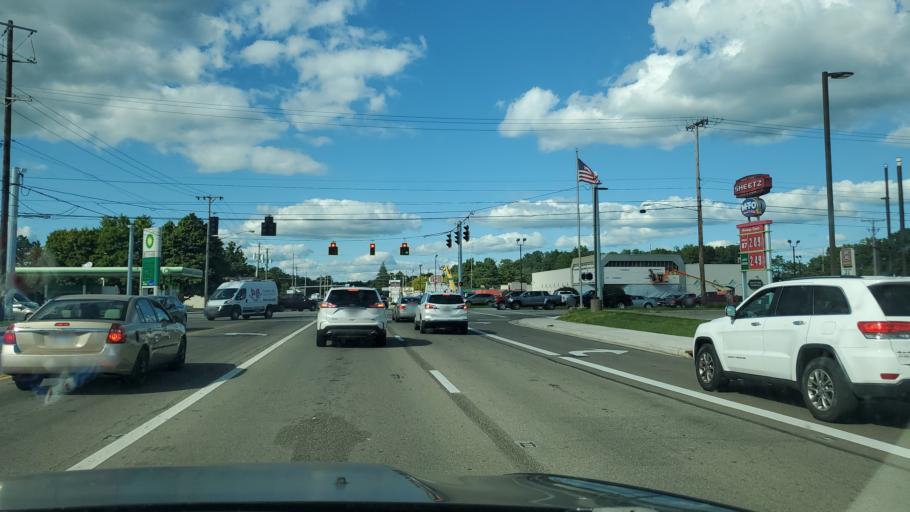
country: US
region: Ohio
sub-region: Mahoning County
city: Austintown
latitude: 41.0990
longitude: -80.7638
